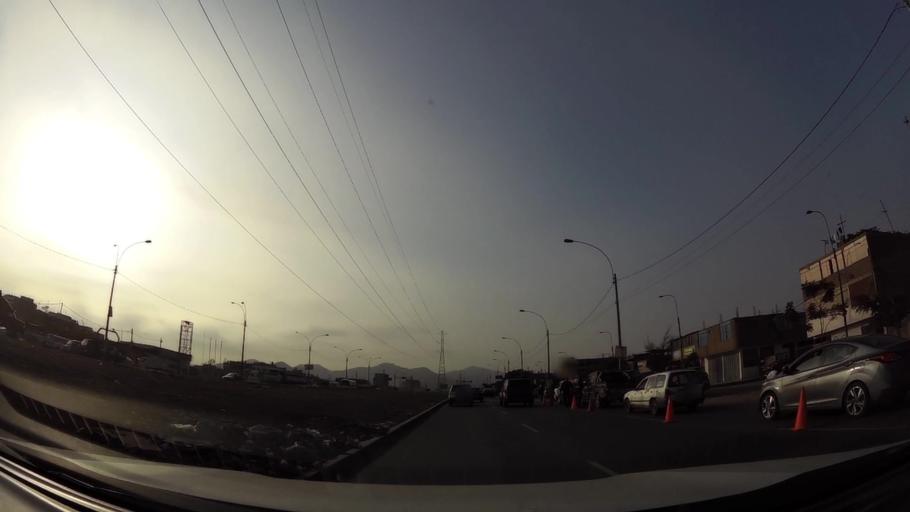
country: PE
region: Lima
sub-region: Lima
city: Independencia
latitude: -11.9636
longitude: -77.0834
